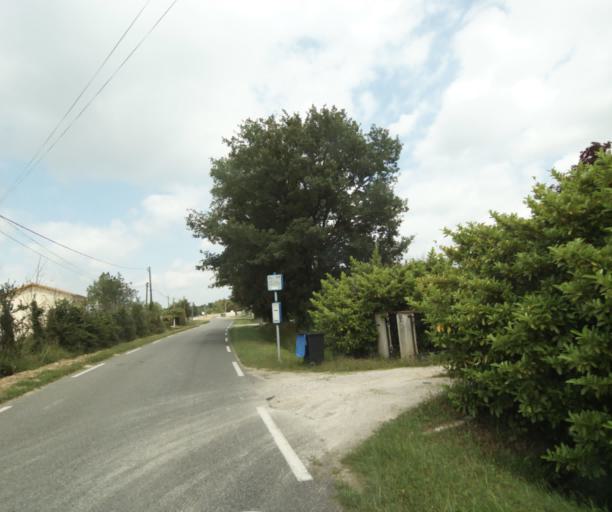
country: FR
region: Midi-Pyrenees
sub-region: Departement du Tarn-et-Garonne
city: Montauban
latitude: 44.0525
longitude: 1.3887
